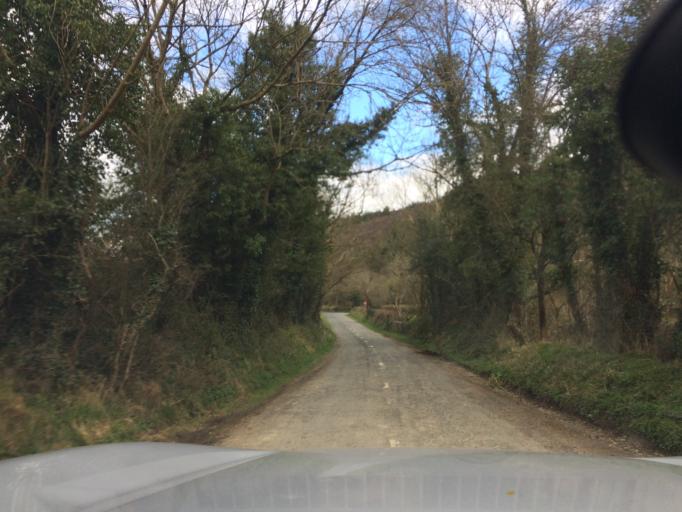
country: IE
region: Munster
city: Carrick-on-Suir
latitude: 52.2818
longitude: -7.4164
